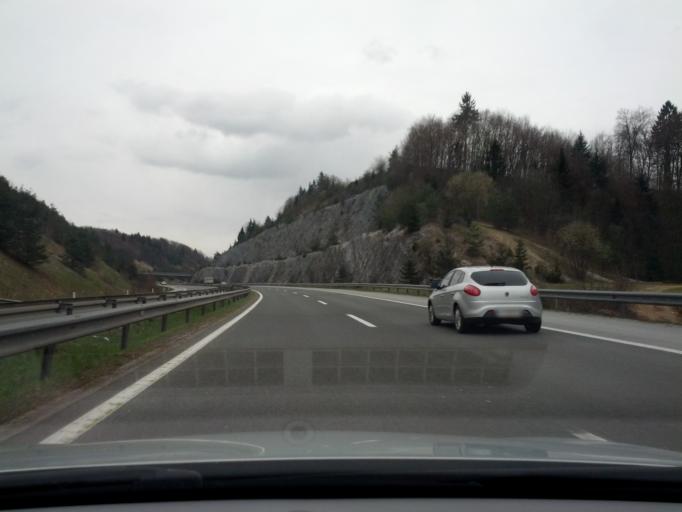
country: SI
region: Skofljica
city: Skofljica
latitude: 45.9989
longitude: 14.5845
